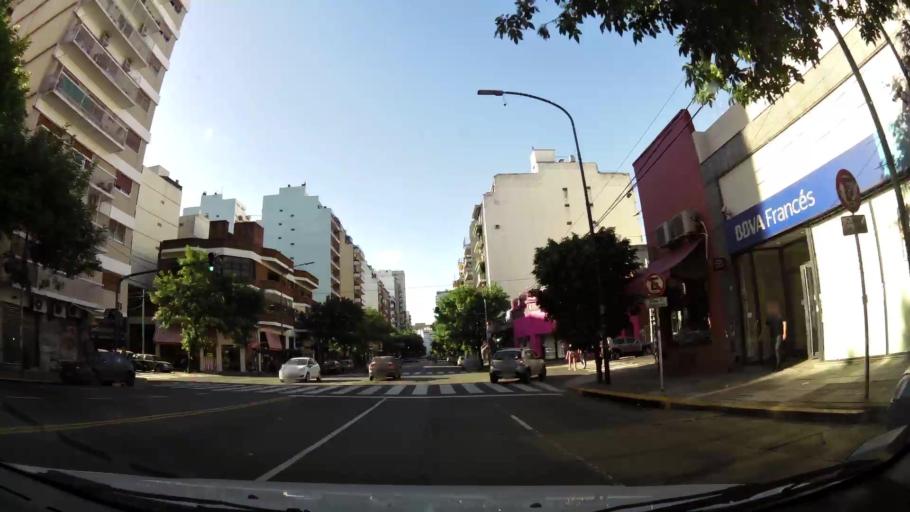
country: AR
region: Buenos Aires F.D.
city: Buenos Aires
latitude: -34.6209
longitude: -58.4280
